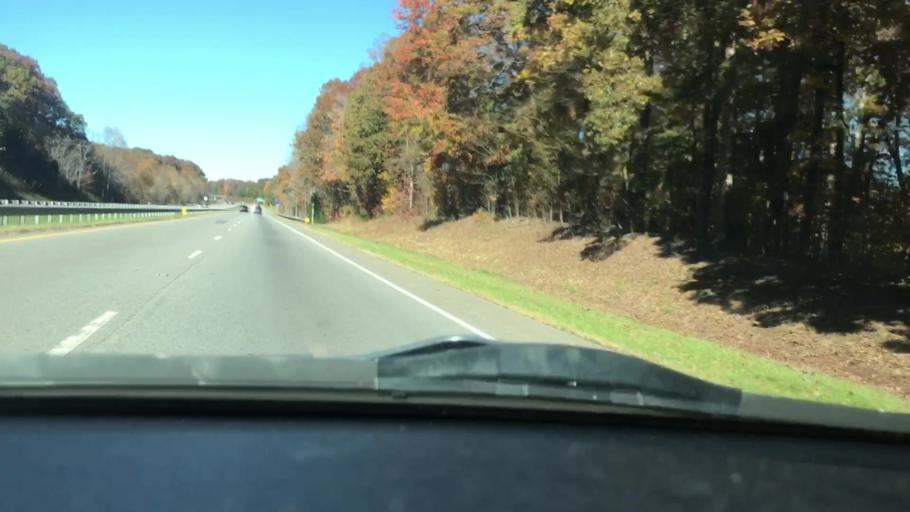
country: US
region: North Carolina
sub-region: Rockingham County
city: Madison
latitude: 36.3990
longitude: -79.9393
